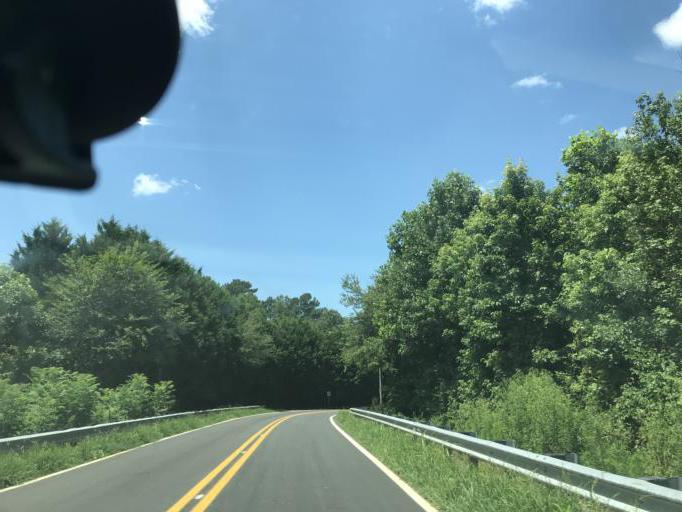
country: US
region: Georgia
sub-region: Forsyth County
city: Cumming
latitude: 34.2683
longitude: -84.2525
